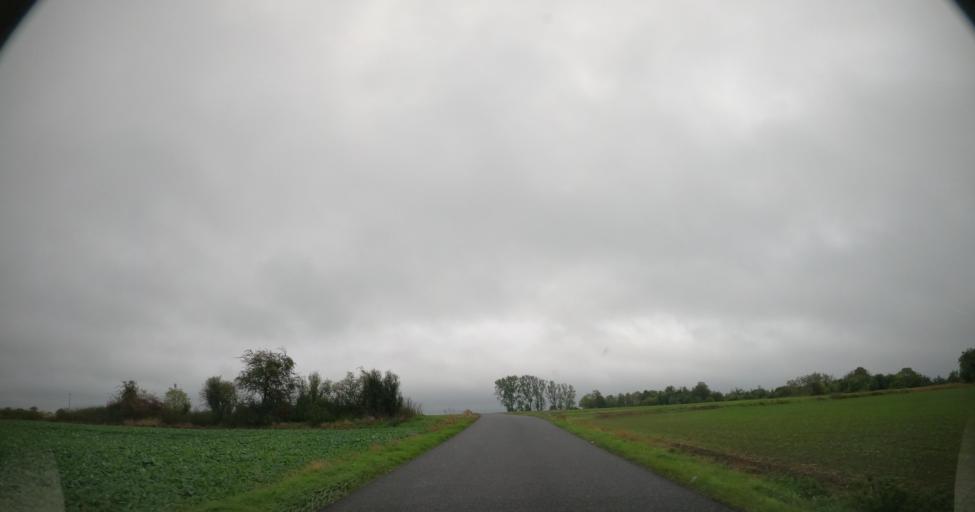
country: PL
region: West Pomeranian Voivodeship
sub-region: Powiat pyrzycki
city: Kozielice
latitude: 53.1191
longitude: 14.7576
